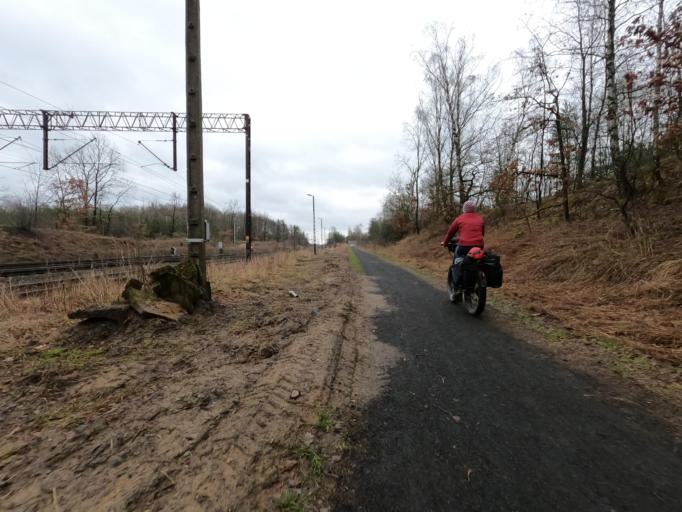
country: PL
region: Greater Poland Voivodeship
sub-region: Powiat pilski
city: Kaczory
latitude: 53.1072
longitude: 16.8757
